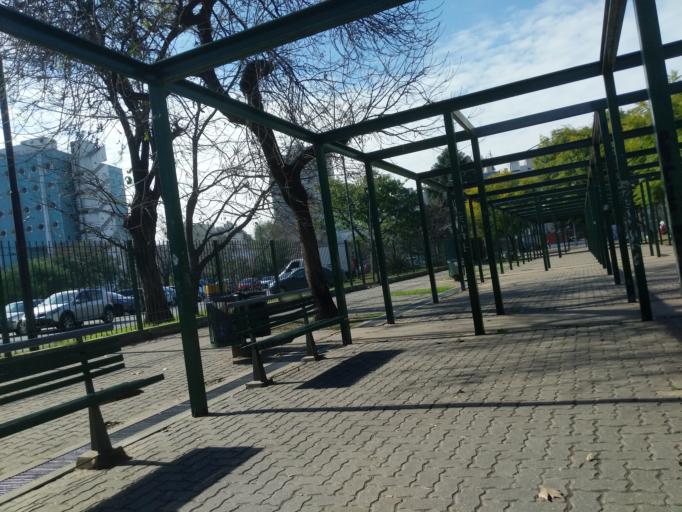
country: AR
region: Buenos Aires F.D.
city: Colegiales
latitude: -34.6065
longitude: -58.4339
